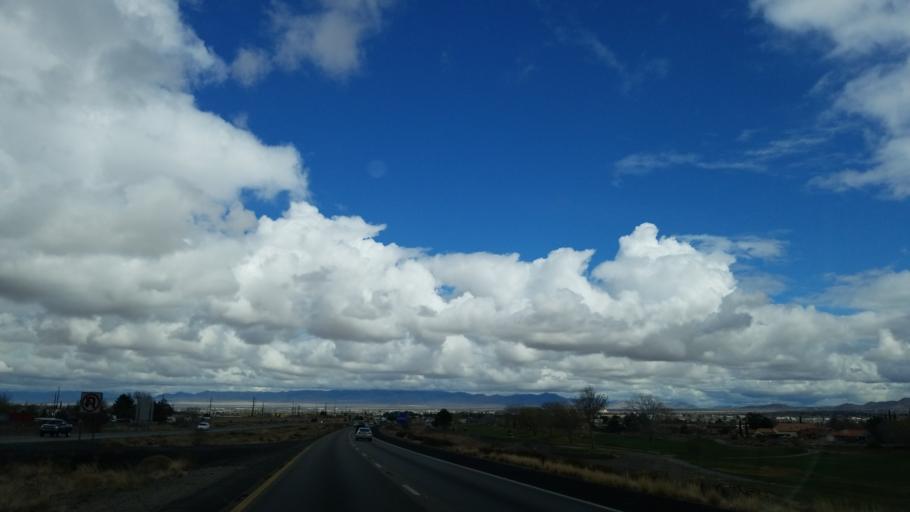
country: US
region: Arizona
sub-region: Mohave County
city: Kingman
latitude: 35.2124
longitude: -114.0510
